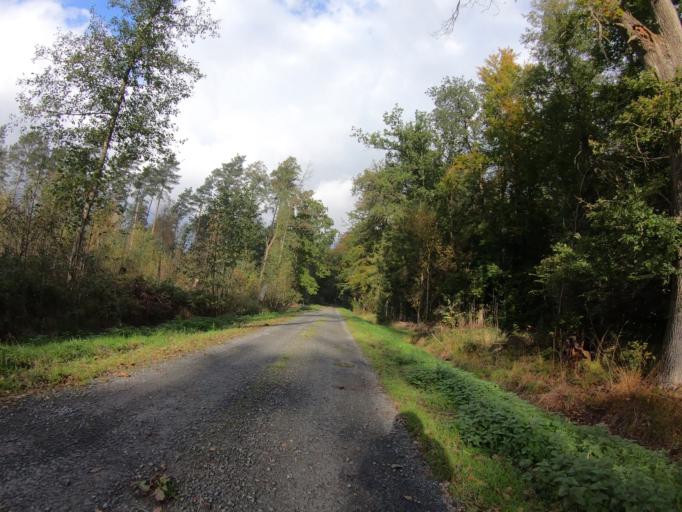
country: DE
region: Lower Saxony
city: Wahrenholz
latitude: 52.5899
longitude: 10.6300
